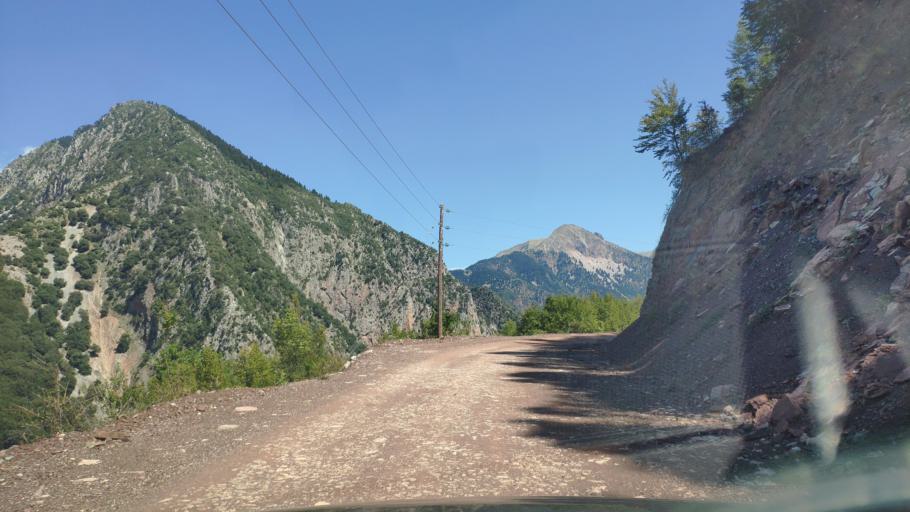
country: GR
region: Central Greece
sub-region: Nomos Evrytanias
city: Kerasochori
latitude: 39.1071
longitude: 21.6086
